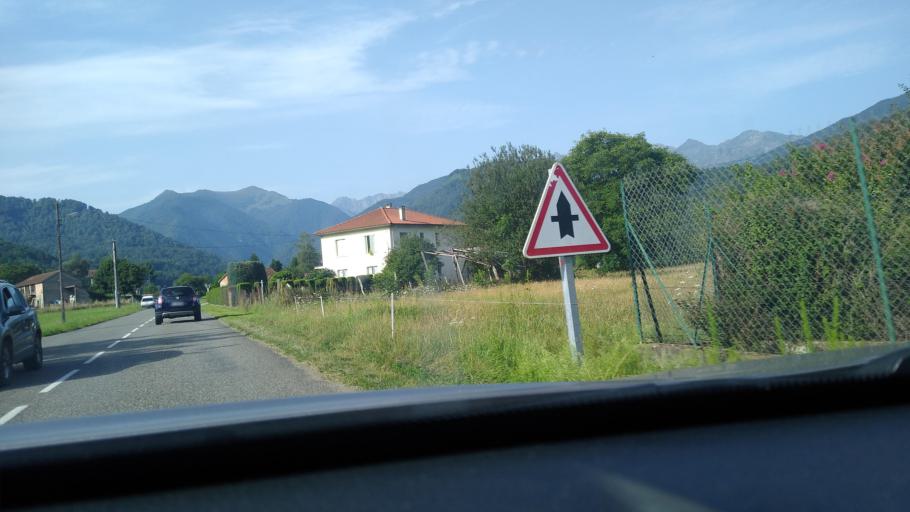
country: FR
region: Midi-Pyrenees
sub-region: Departement de l'Ariege
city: Saint-Girons
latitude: 42.8769
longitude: 1.2136
